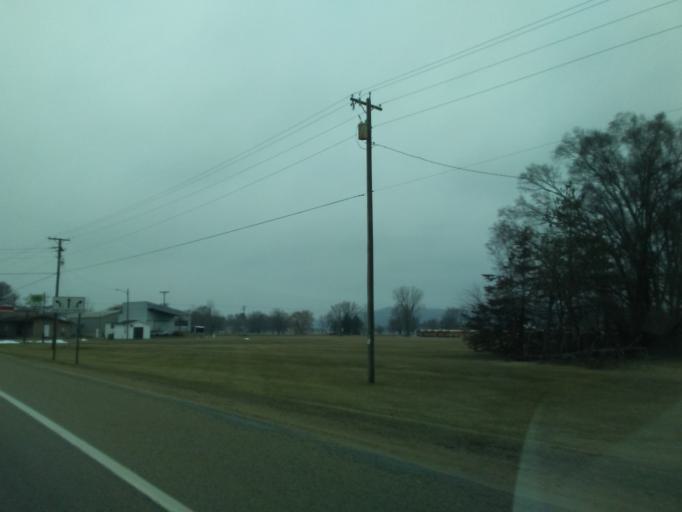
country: US
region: Wisconsin
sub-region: Sauk County
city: Spring Green
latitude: 43.1895
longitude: -90.0714
